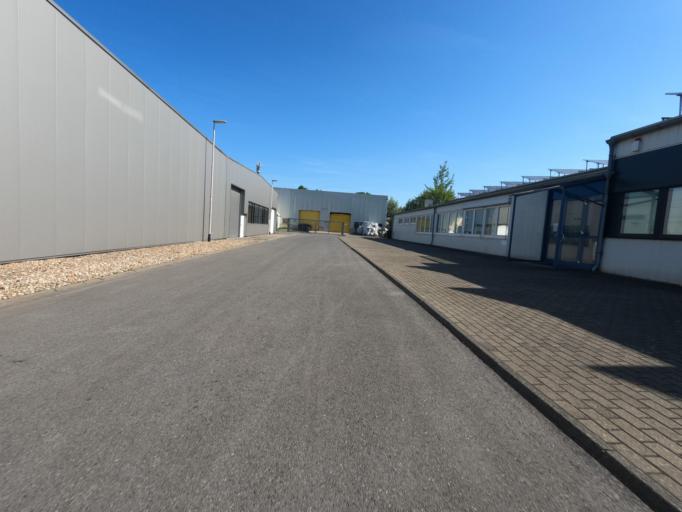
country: DE
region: North Rhine-Westphalia
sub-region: Regierungsbezirk Koln
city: Heinsberg
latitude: 51.0667
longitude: 6.1192
